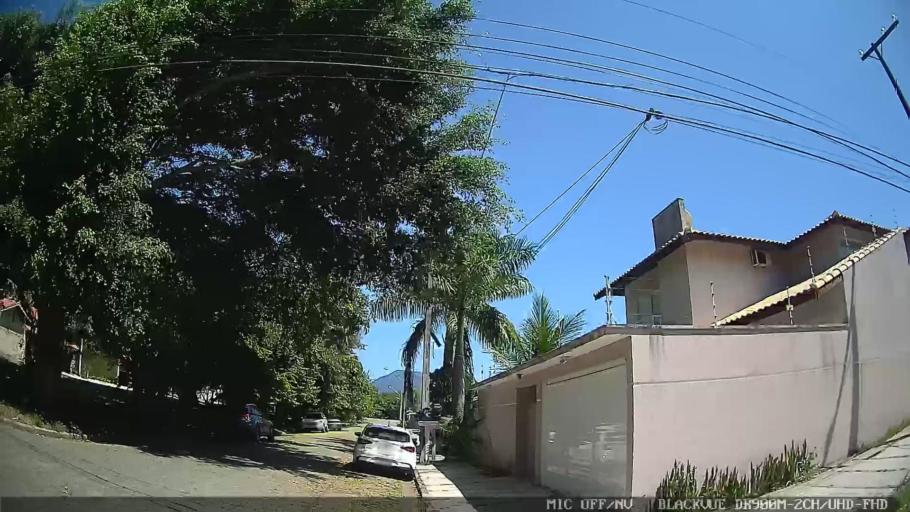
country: BR
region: Sao Paulo
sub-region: Peruibe
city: Peruibe
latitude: -24.3006
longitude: -46.9757
